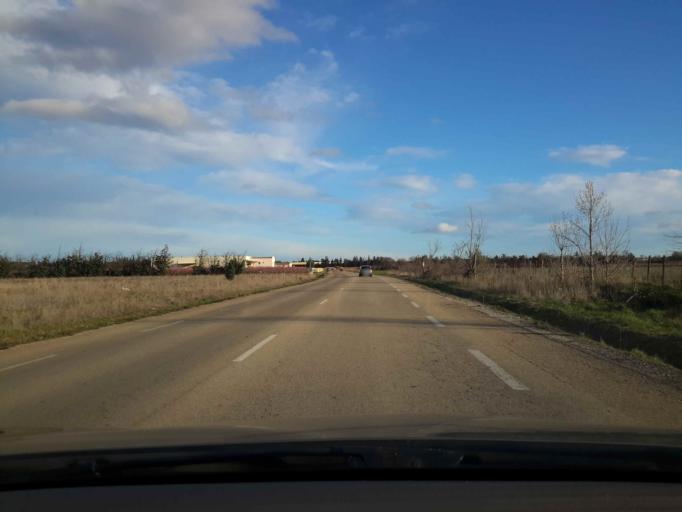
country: FR
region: Languedoc-Roussillon
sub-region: Departement du Gard
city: Aubord
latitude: 43.7625
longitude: 4.3337
